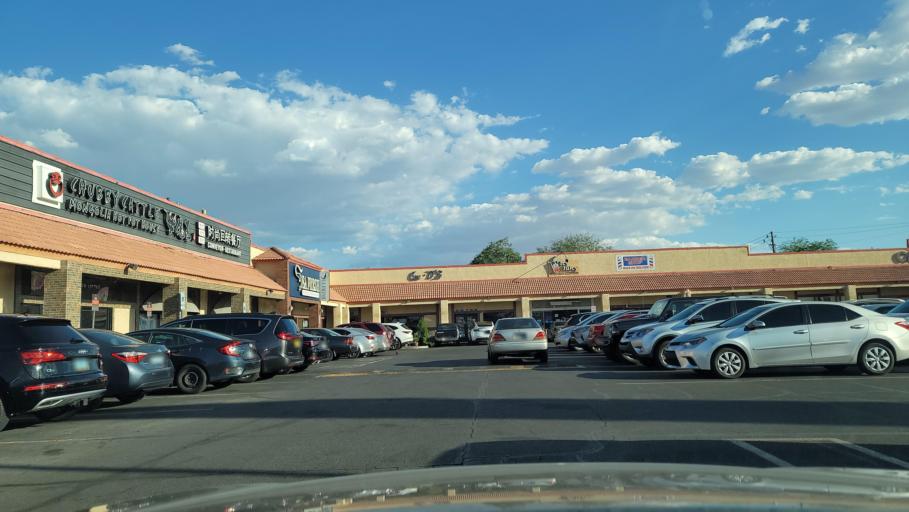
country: US
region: Nevada
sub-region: Clark County
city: Spring Valley
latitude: 36.1271
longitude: -115.2243
